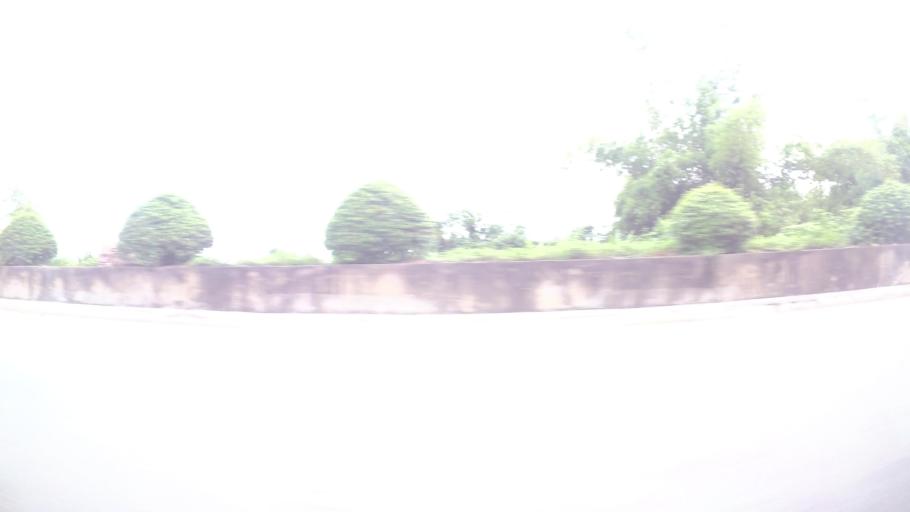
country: VN
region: Ha Noi
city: Trau Quy
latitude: 21.0771
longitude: 105.9006
